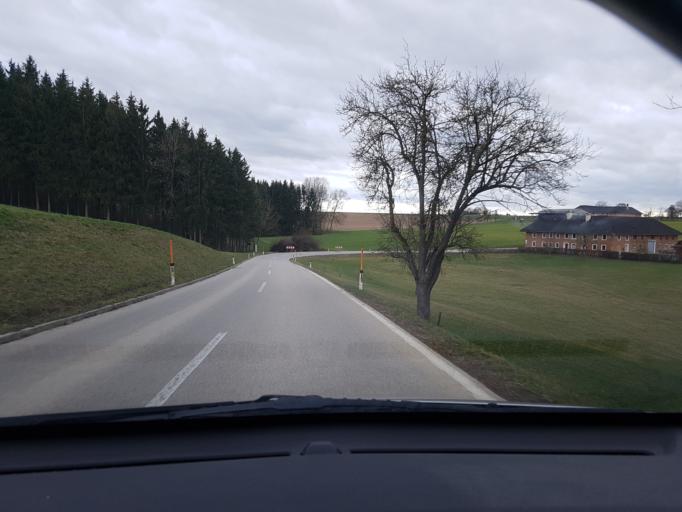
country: AT
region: Upper Austria
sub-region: Politischer Bezirk Linz-Land
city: Ansfelden
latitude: 48.1635
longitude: 14.3135
